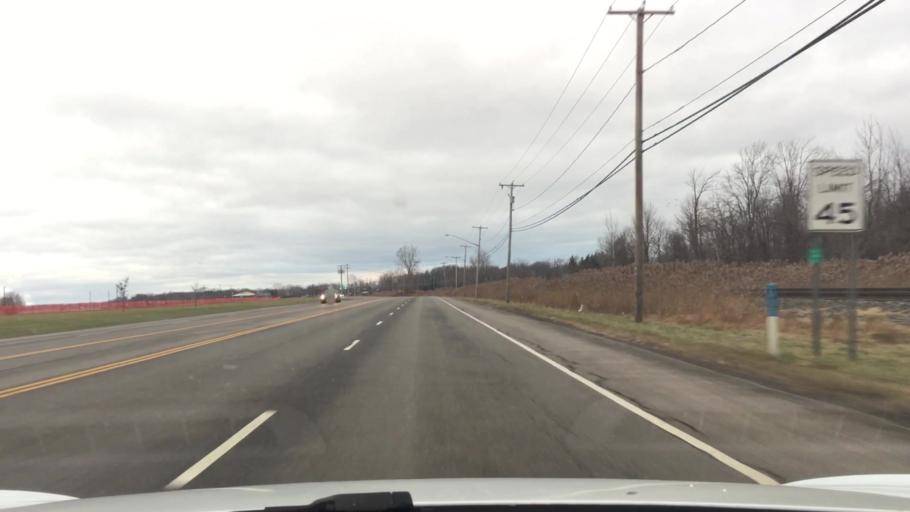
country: US
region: New York
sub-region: Niagara County
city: North Tonawanda
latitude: 43.0524
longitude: -78.8944
